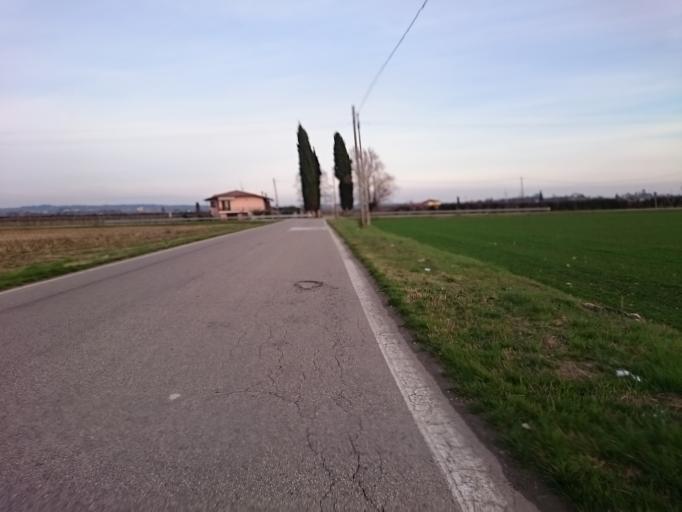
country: IT
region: Veneto
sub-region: Provincia di Verona
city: Cola
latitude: 45.4569
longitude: 10.7413
